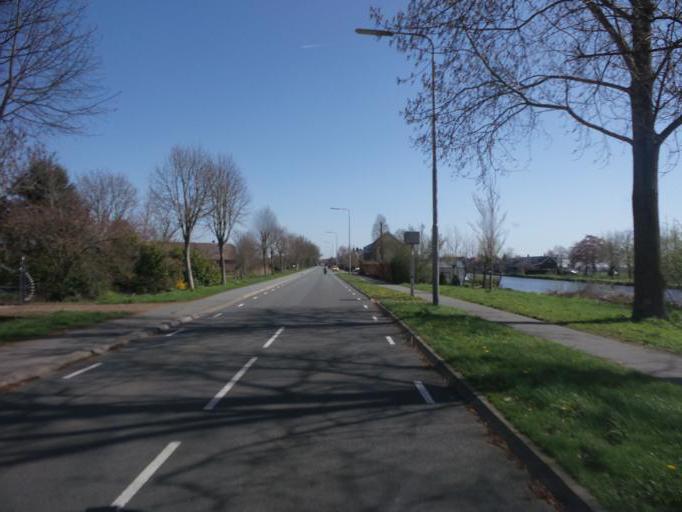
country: NL
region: South Holland
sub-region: Bodegraven-Reeuwijk
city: Bodegraven
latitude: 52.0817
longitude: 4.8044
